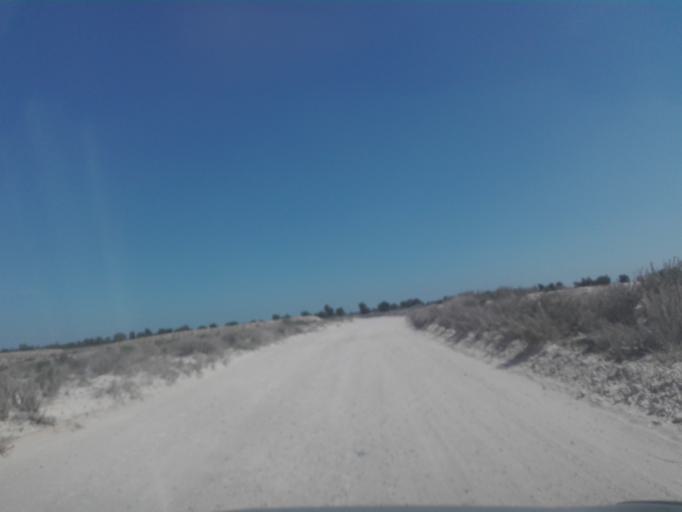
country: TN
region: Qabis
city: Gabes
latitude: 33.8701
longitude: 10.0105
